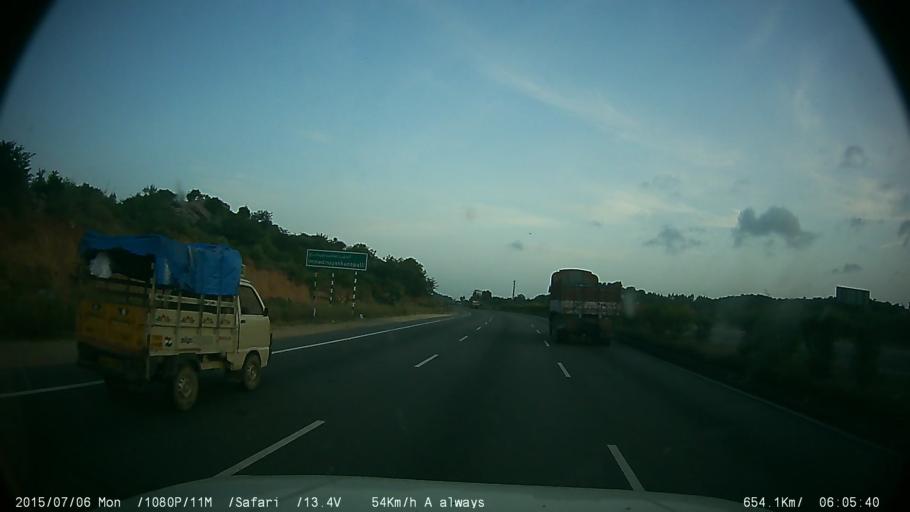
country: IN
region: Tamil Nadu
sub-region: Krishnagiri
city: Krishnagiri
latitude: 12.6260
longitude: 78.0796
